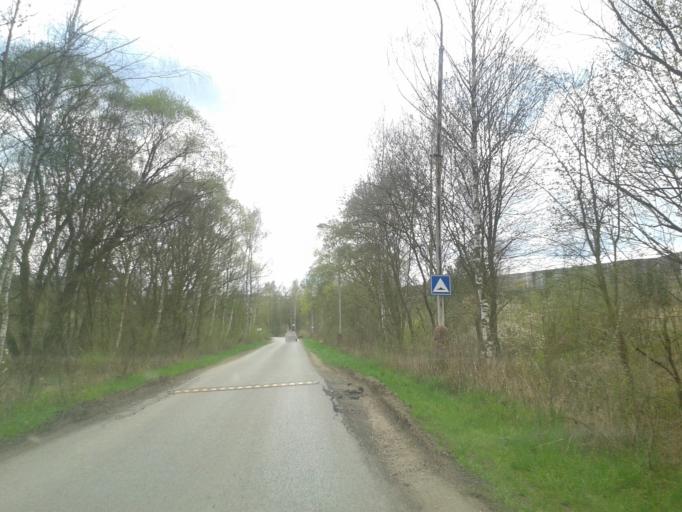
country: CZ
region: Central Bohemia
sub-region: Okres Beroun
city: Lodenice
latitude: 49.9977
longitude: 14.1674
